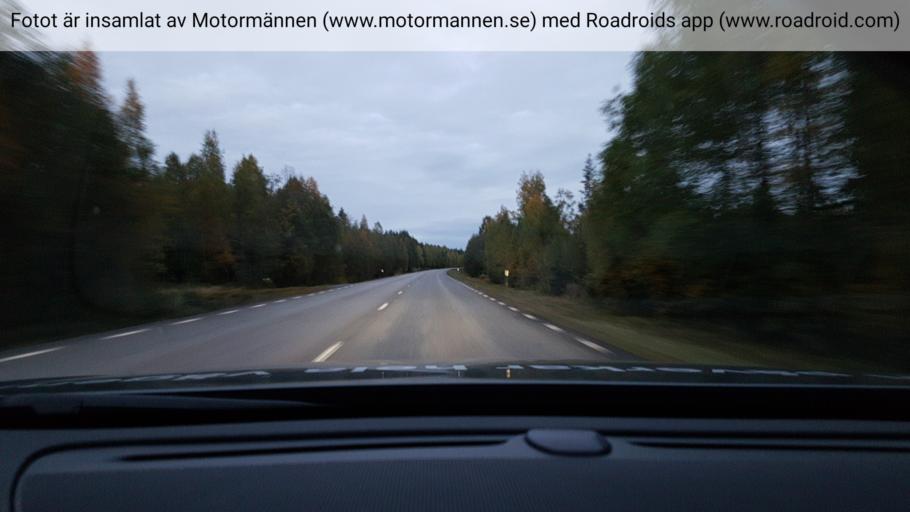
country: SE
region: Norrbotten
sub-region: Alvsbyns Kommun
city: AElvsbyn
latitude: 65.7813
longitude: 20.8154
